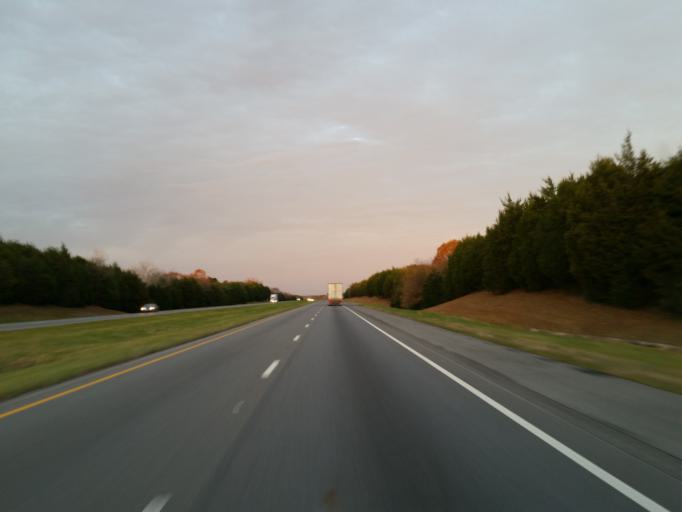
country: US
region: Alabama
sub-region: Sumter County
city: Livingston
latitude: 32.6586
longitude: -88.1840
